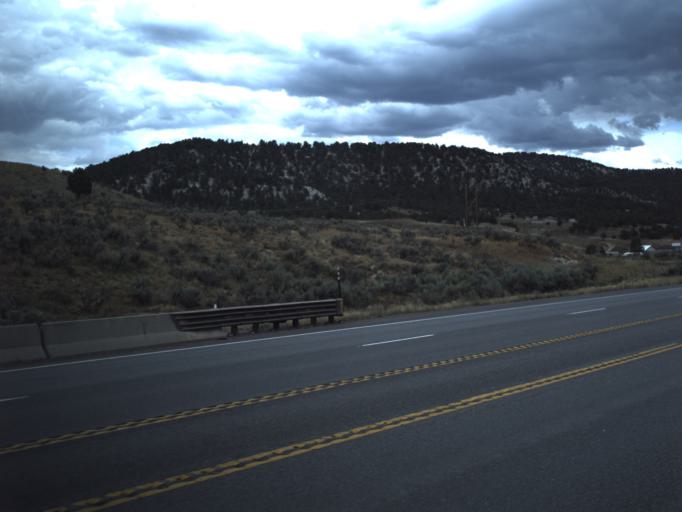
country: US
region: Utah
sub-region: Utah County
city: Mapleton
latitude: 39.9751
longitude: -111.3418
